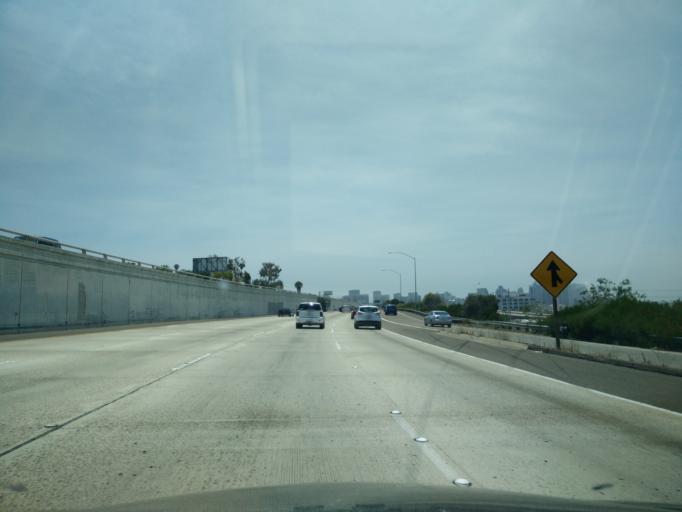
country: US
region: California
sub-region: San Diego County
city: San Diego
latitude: 32.7410
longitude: -117.1801
